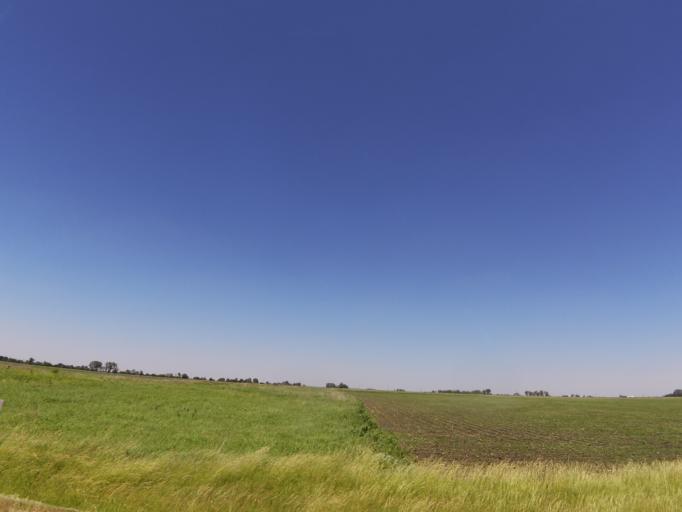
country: US
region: Illinois
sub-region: Livingston County
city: Chatsworth
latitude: 40.7484
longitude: -88.1726
